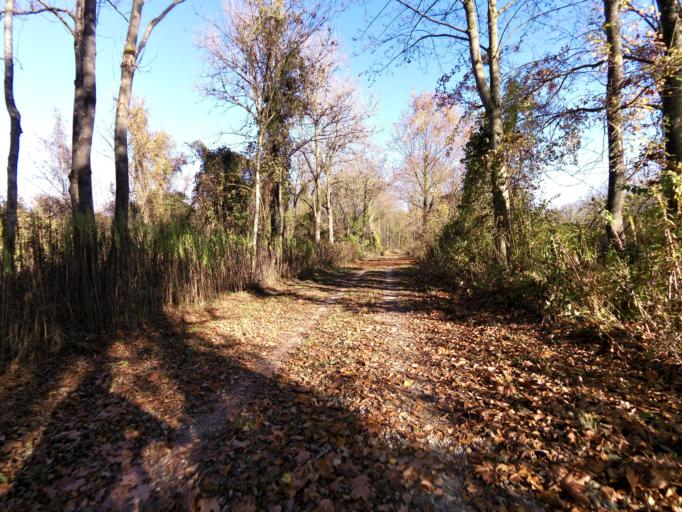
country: DE
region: Bavaria
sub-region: Lower Bavaria
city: Bruckberg
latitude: 48.5014
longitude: 12.0214
